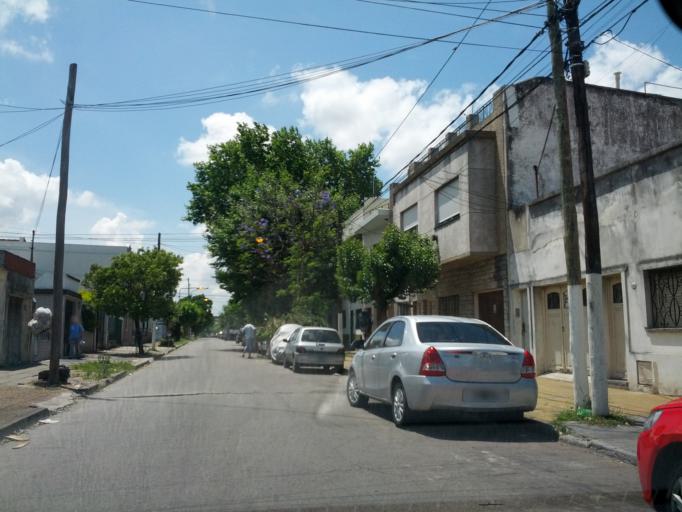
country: AR
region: Buenos Aires
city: San Justo
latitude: -34.6435
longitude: -58.5402
